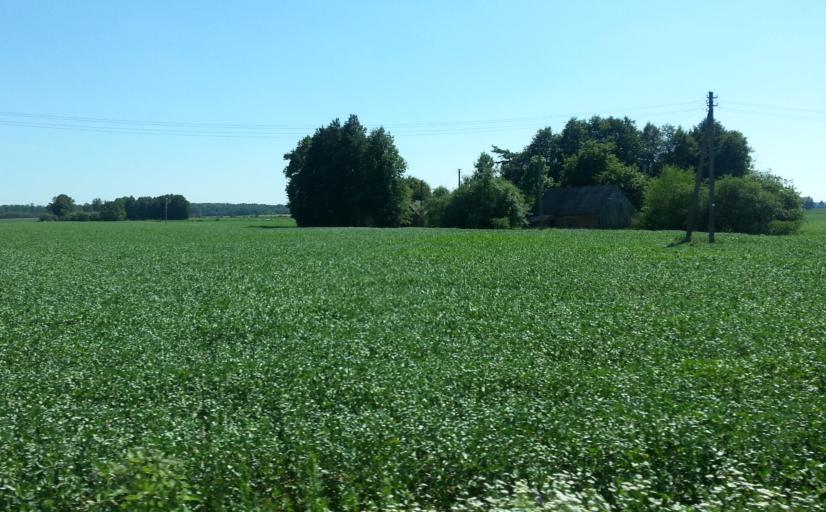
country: LT
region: Panevezys
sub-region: Birzai
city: Birzai
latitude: 56.2304
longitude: 24.5941
